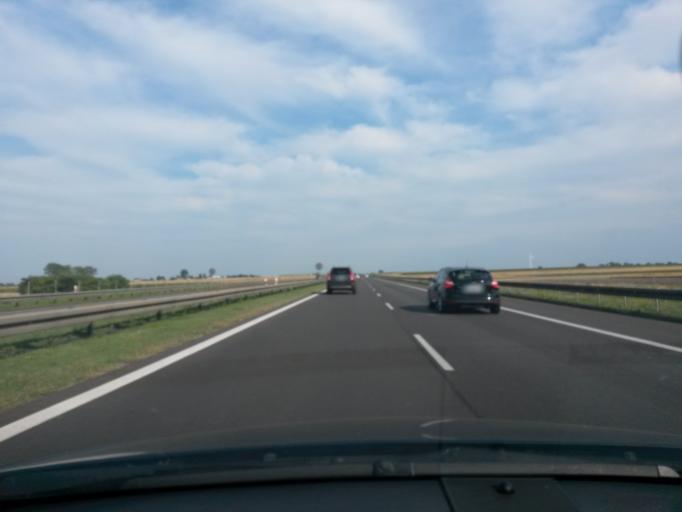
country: PL
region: Greater Poland Voivodeship
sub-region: Powiat slupecki
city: Ladek
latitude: 52.2193
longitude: 17.9599
